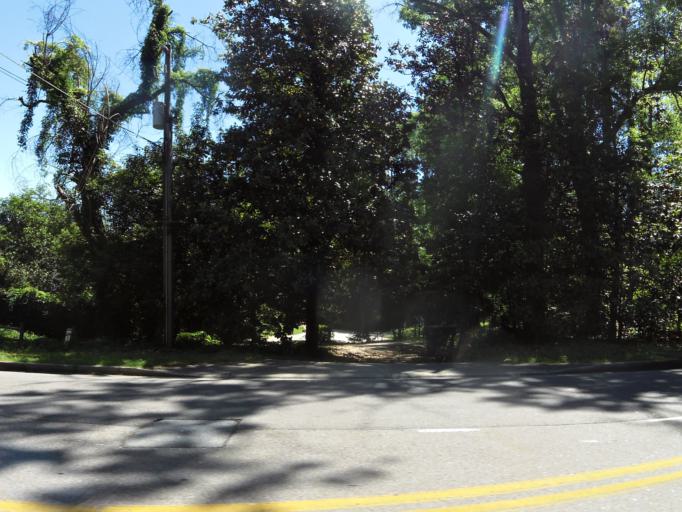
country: US
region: Georgia
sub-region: Columbia County
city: Martinez
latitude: 33.4932
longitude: -82.0303
